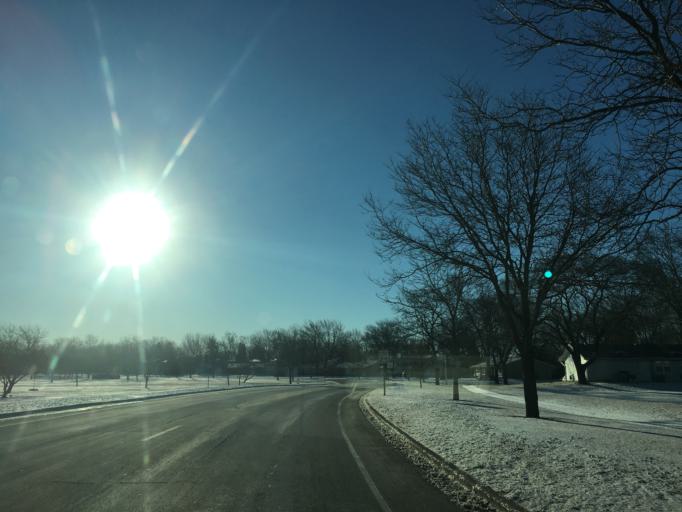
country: US
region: Illinois
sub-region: Cook County
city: Schaumburg
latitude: 42.0185
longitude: -88.1090
